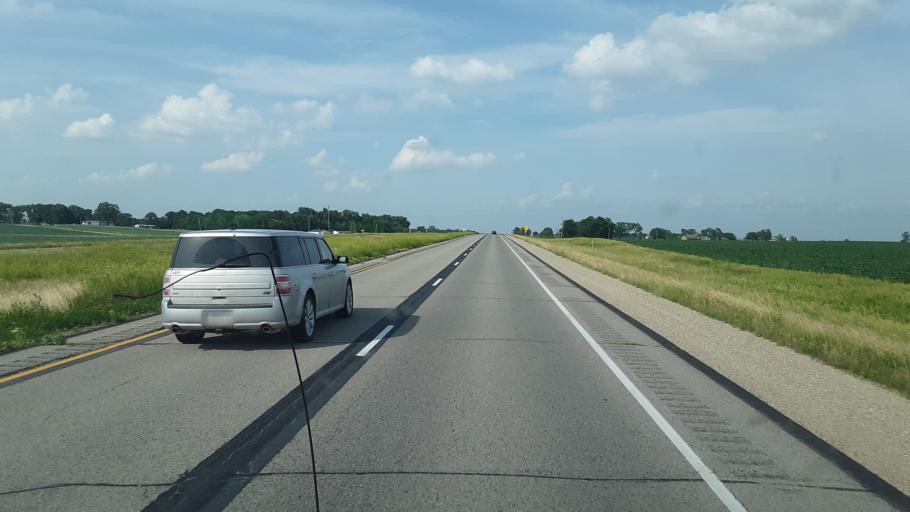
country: US
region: Iowa
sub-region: Jasper County
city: Baxter
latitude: 41.8463
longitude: -93.2566
